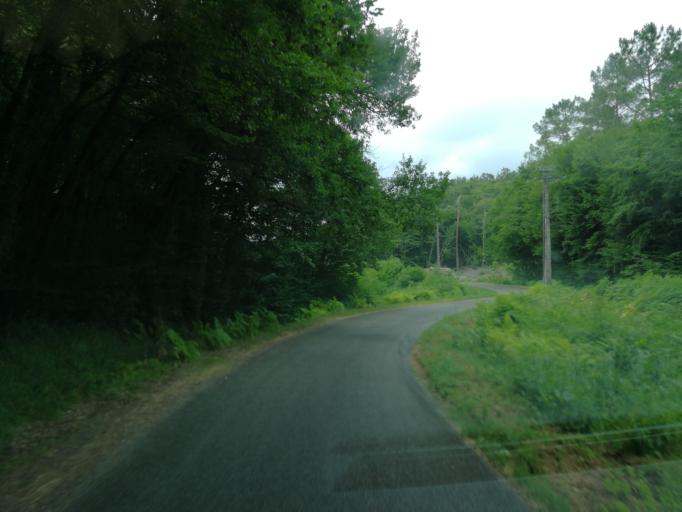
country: FR
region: Aquitaine
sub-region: Departement du Lot-et-Garonne
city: Montayral
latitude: 44.5547
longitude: 1.0725
